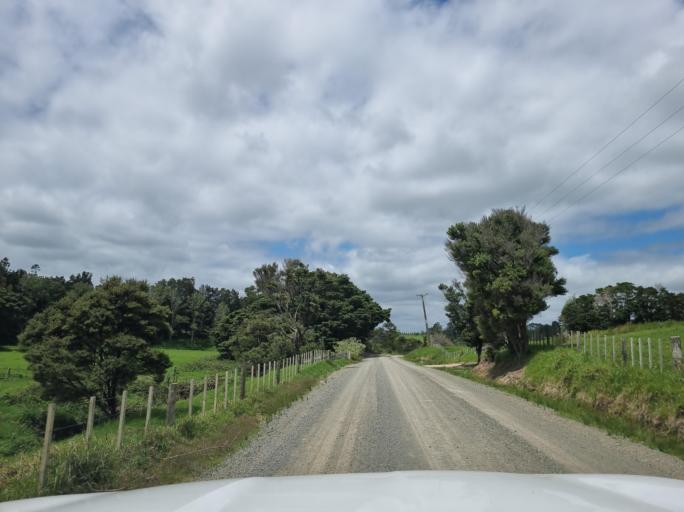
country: NZ
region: Northland
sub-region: Whangarei
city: Ruakaka
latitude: -36.0790
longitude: 174.5507
